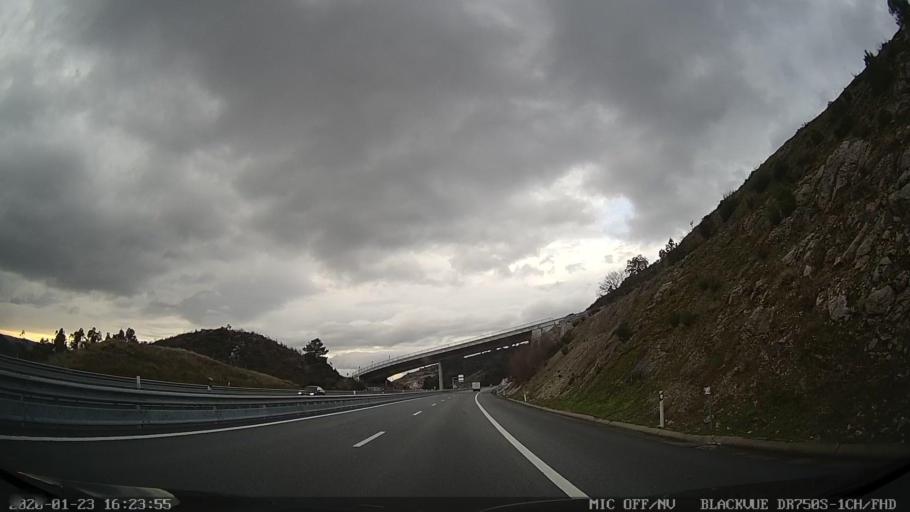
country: PT
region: Porto
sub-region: Baiao
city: Valadares
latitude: 41.2515
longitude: -7.9689
